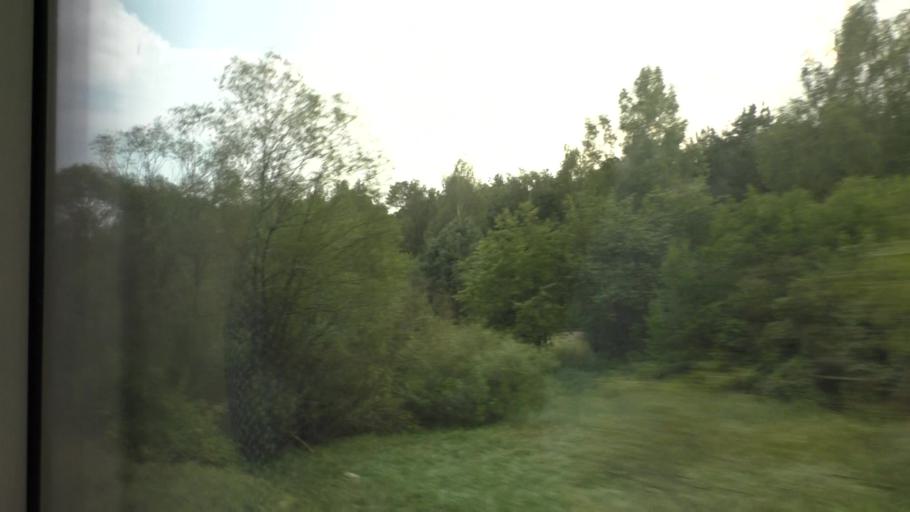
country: DE
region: Brandenburg
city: Wendisch Rietz
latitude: 52.2132
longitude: 13.9999
